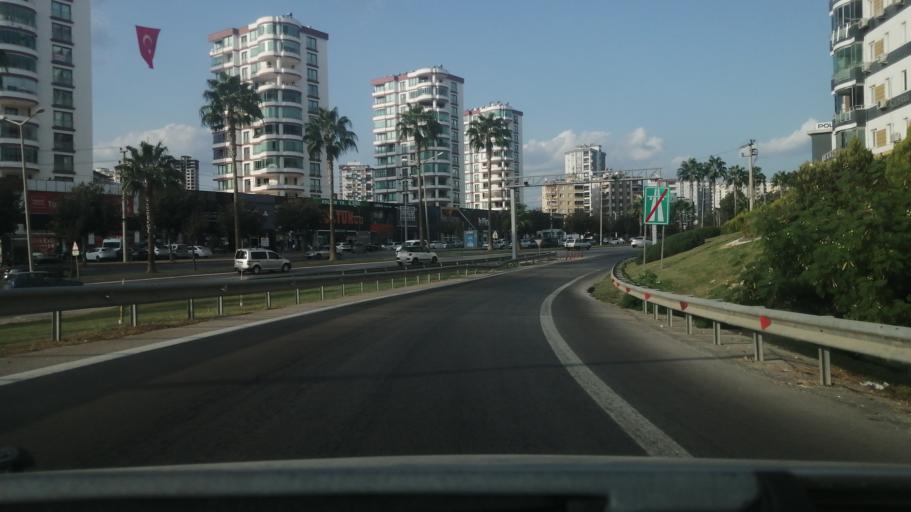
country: TR
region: Adana
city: Seyhan
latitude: 37.0333
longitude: 35.2561
